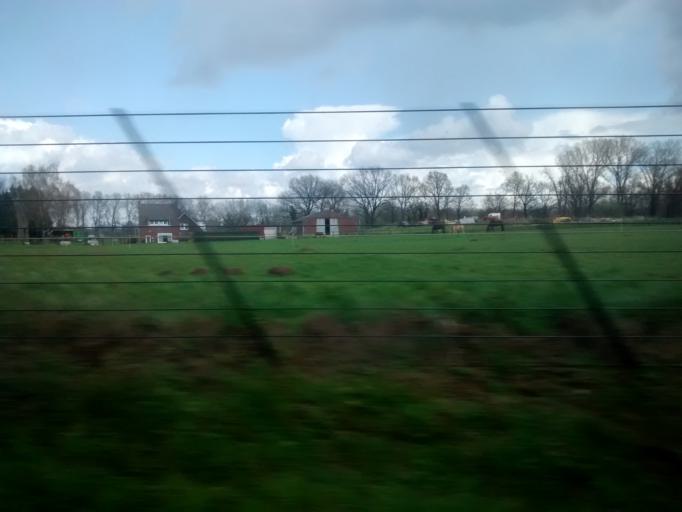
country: NL
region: Limburg
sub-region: Gemeente Roermond
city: Leeuwen
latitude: 51.2127
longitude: 6.0019
